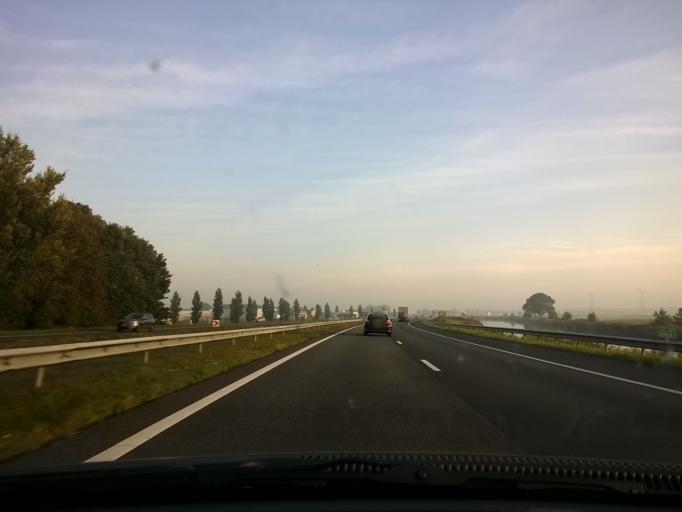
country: NL
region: Friesland
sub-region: Gemeente Lemsterland
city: Lemmer
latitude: 52.8508
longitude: 5.7216
